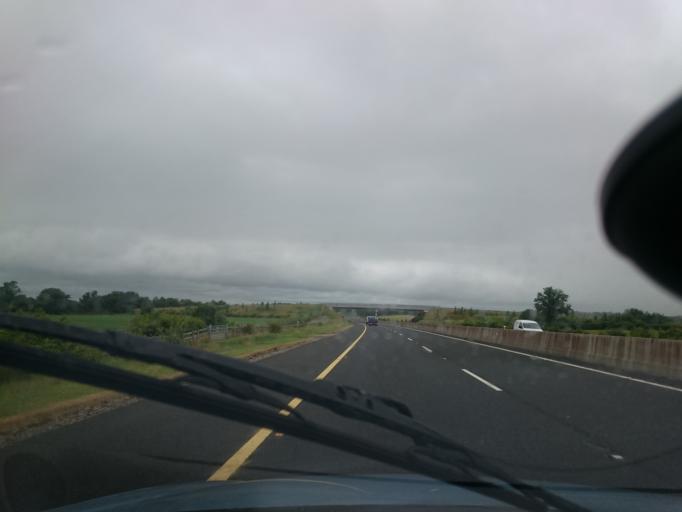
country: IE
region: Leinster
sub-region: Kildare
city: Castledermot
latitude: 52.9384
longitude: -6.8560
